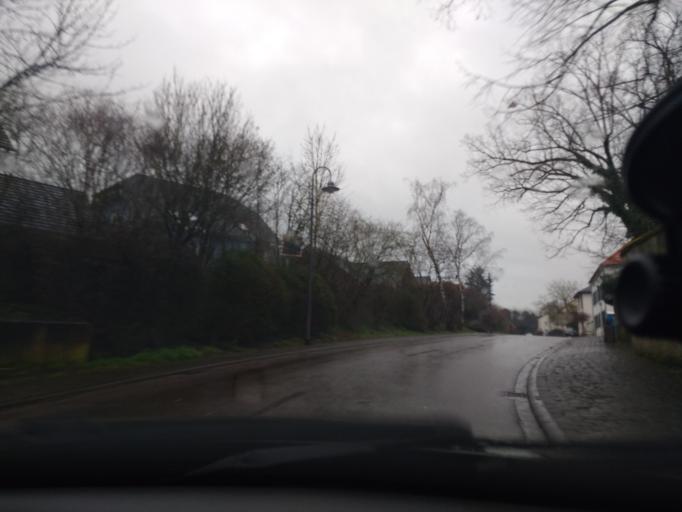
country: DE
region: Rheinland-Pfalz
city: Wawern
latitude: 49.6541
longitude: 6.5503
